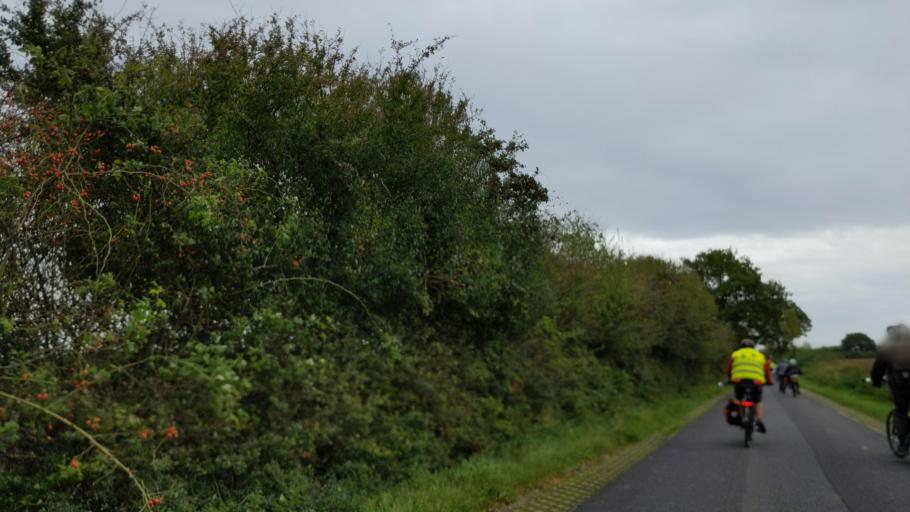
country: DE
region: Schleswig-Holstein
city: Bak
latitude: 53.7310
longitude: 10.7753
